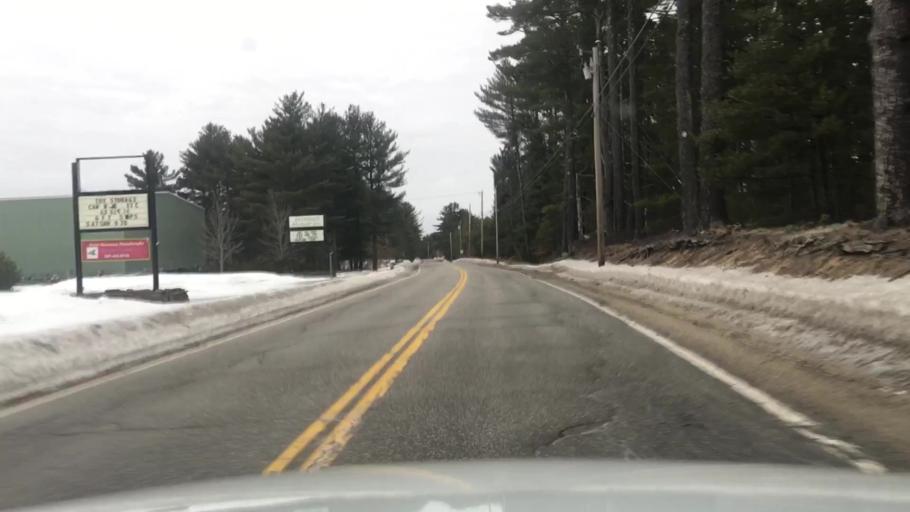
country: US
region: Maine
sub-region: York County
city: Shapleigh
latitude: 43.5619
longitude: -70.8575
